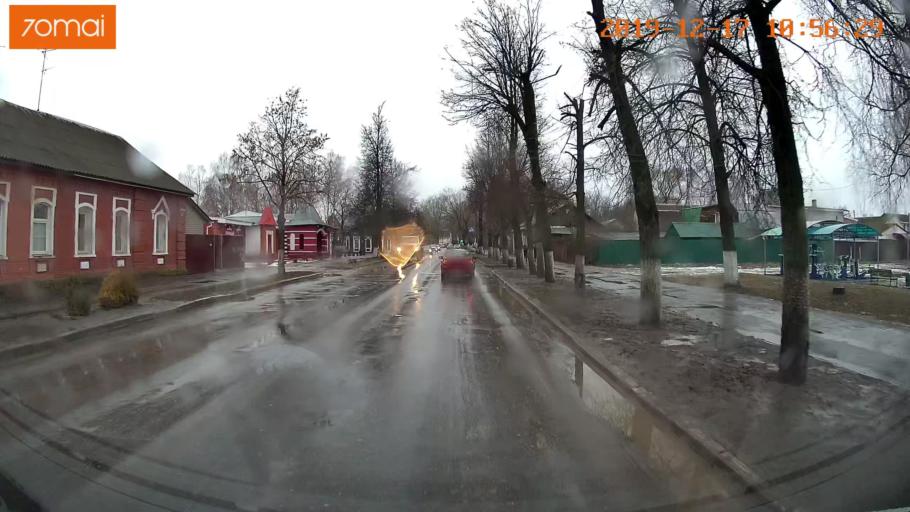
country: RU
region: Vladimir
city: Gus'-Khrustal'nyy
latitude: 55.6182
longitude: 40.6625
